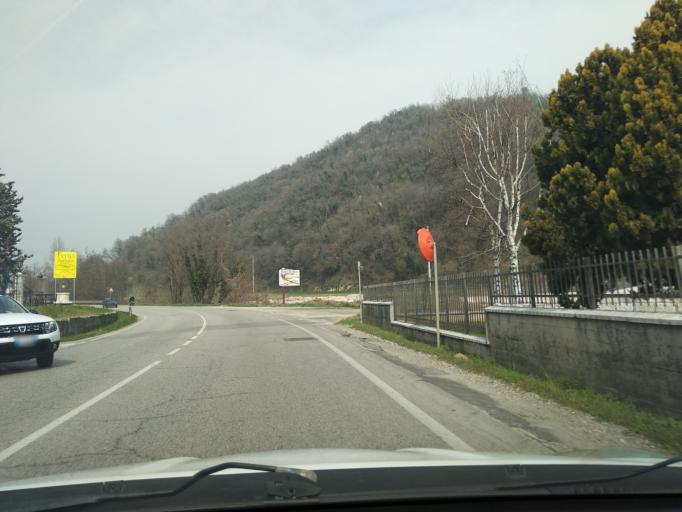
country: IT
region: Veneto
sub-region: Provincia di Vicenza
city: Chiampo
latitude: 45.5571
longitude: 11.2712
